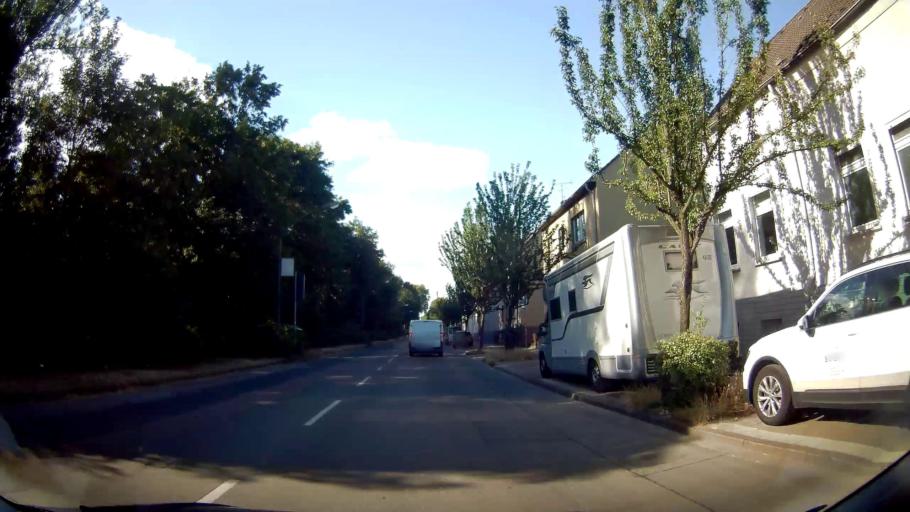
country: DE
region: North Rhine-Westphalia
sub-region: Regierungsbezirk Dusseldorf
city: Essen
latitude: 51.4899
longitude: 6.9805
